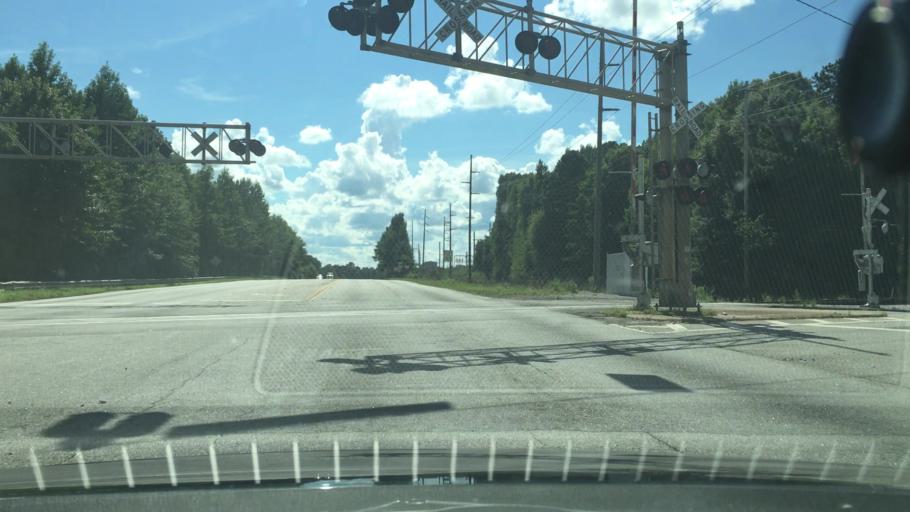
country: US
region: Georgia
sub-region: Spalding County
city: East Griffin
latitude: 33.2334
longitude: -84.2276
